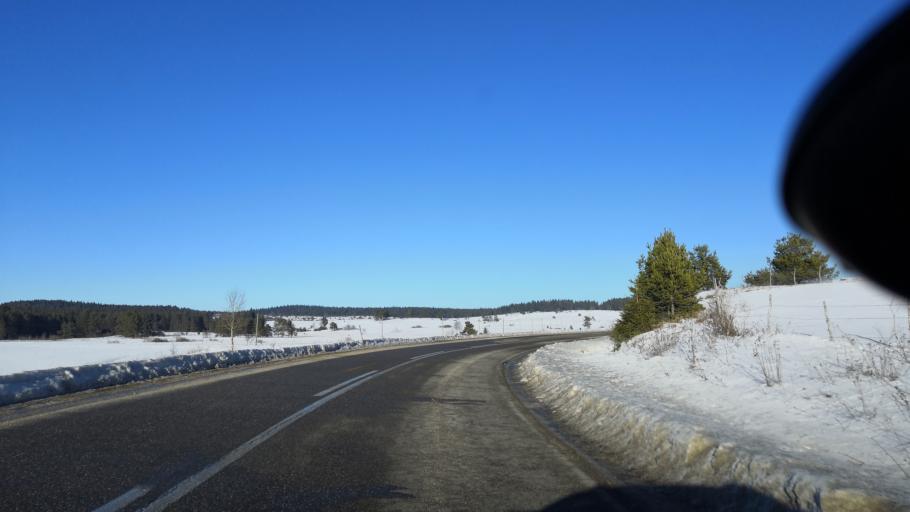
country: BA
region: Republika Srpska
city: Han Pijesak
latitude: 44.0334
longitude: 18.9062
